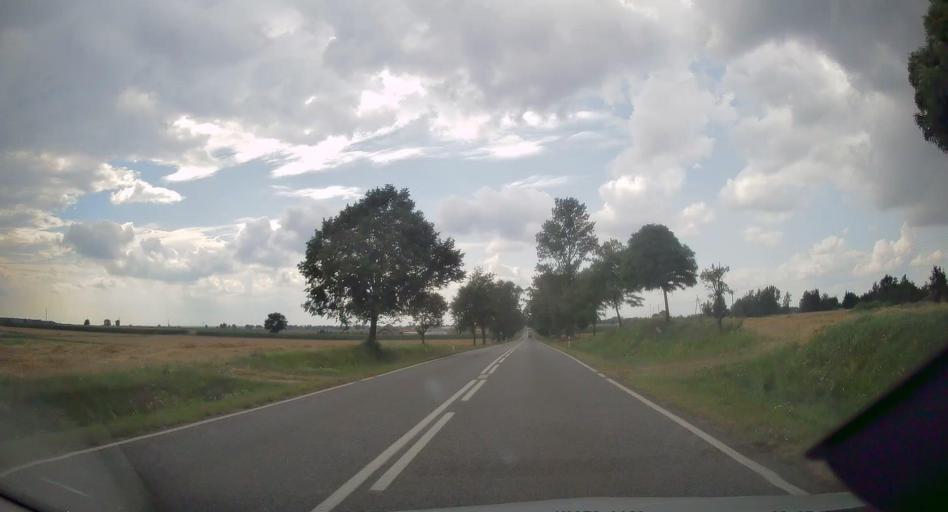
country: PL
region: Lodz Voivodeship
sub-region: Powiat skierniewicki
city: Gluchow
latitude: 51.7777
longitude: 20.1049
